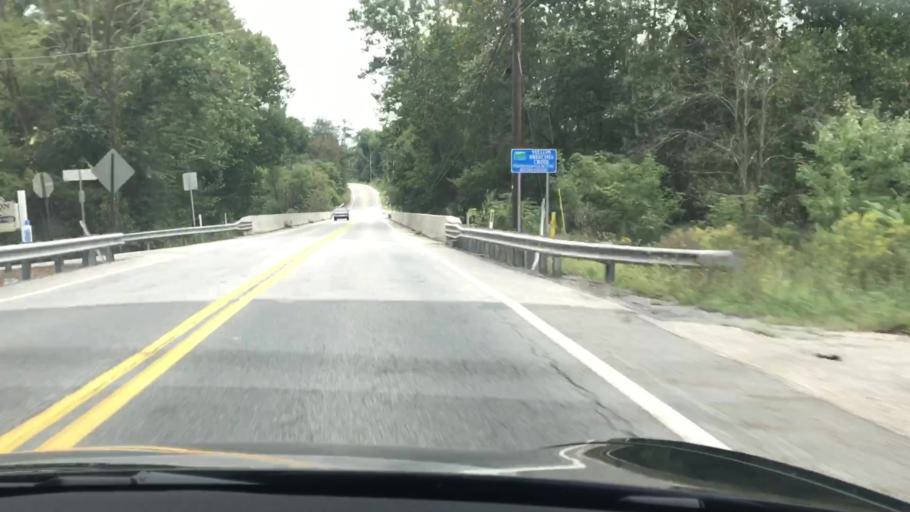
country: US
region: Pennsylvania
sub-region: Cumberland County
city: Mechanicsburg
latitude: 40.1649
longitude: -76.9771
